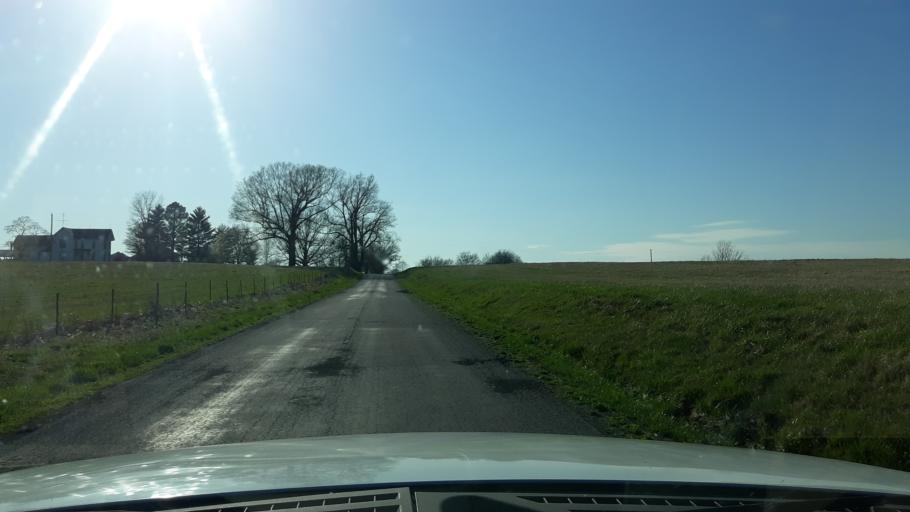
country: US
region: Illinois
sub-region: Saline County
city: Harrisburg
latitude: 37.7645
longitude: -88.5839
